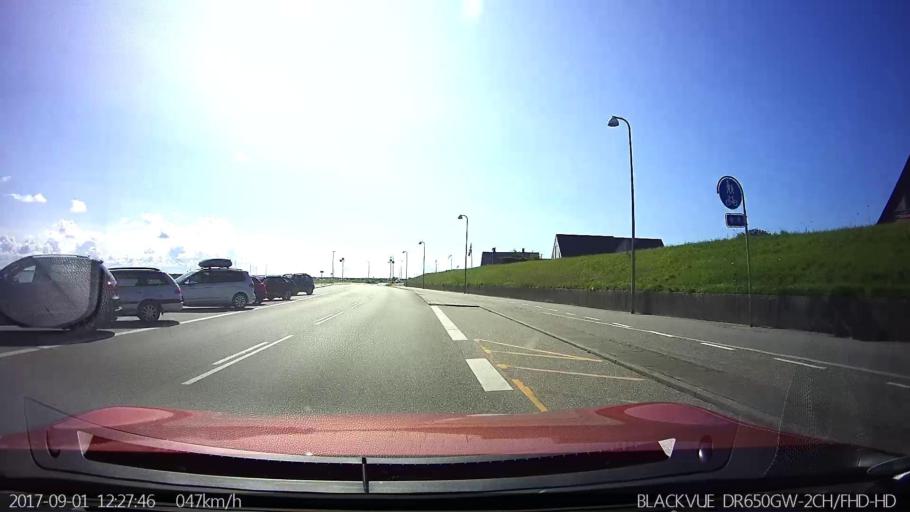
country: DK
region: South Denmark
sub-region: Fano Kommune
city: Nordby
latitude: 55.4463
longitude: 8.4061
